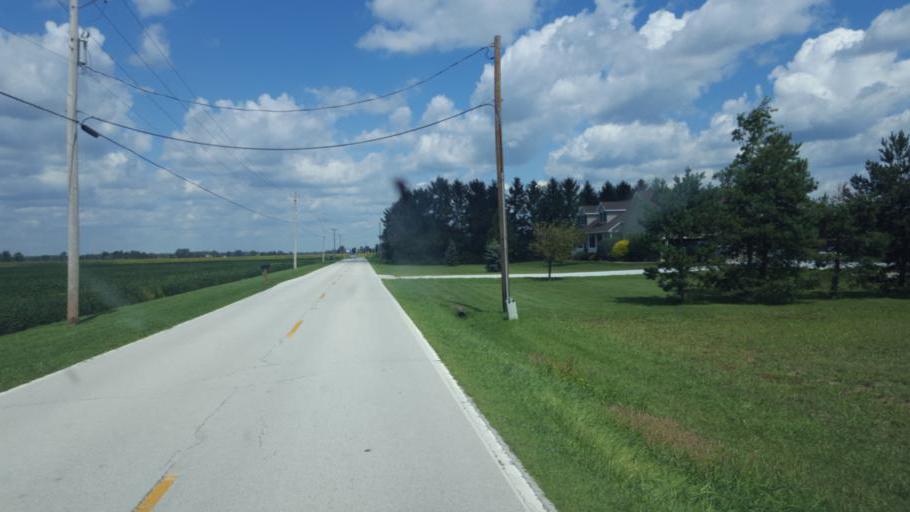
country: US
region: Ohio
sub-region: Sandusky County
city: Gibsonburg
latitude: 41.3312
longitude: -83.3059
